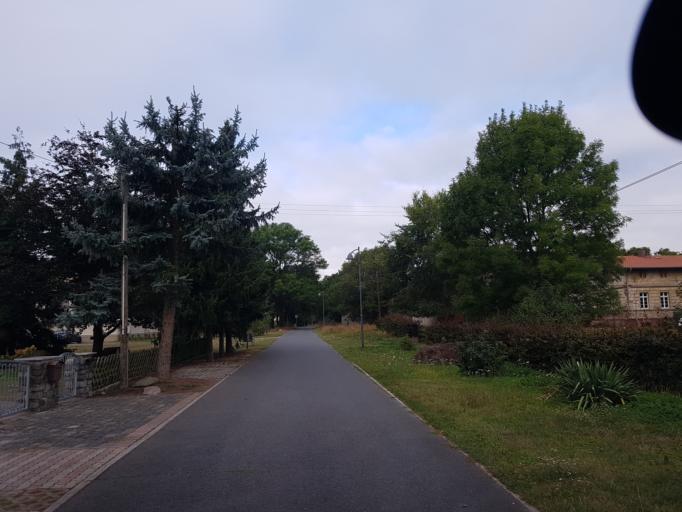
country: DE
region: Brandenburg
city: Calau
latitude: 51.7724
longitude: 13.8766
